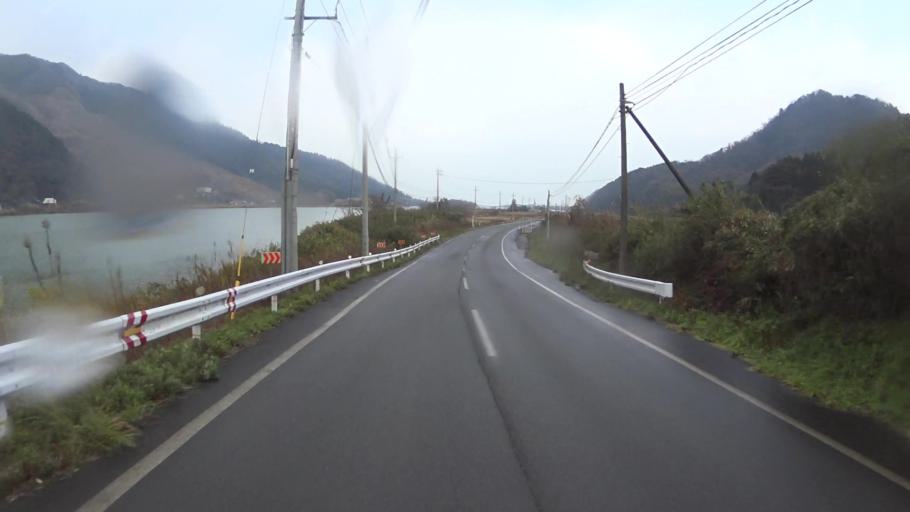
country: JP
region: Kyoto
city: Maizuru
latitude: 35.4823
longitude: 135.2831
